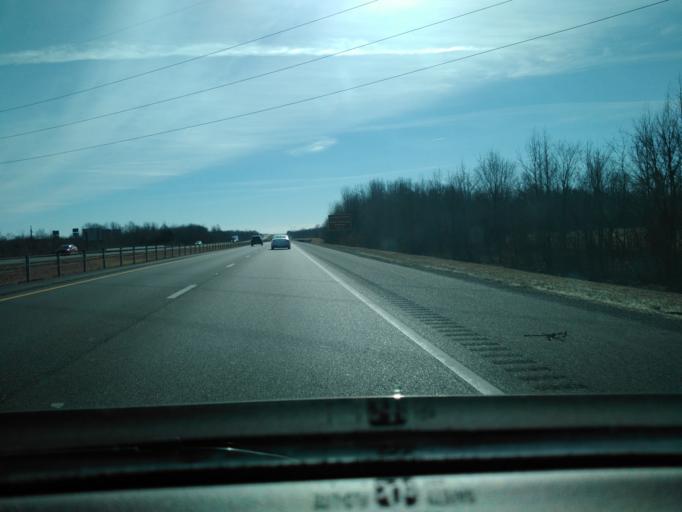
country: US
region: Kentucky
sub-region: McCracken County
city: Hendron
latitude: 37.0314
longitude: -88.6206
